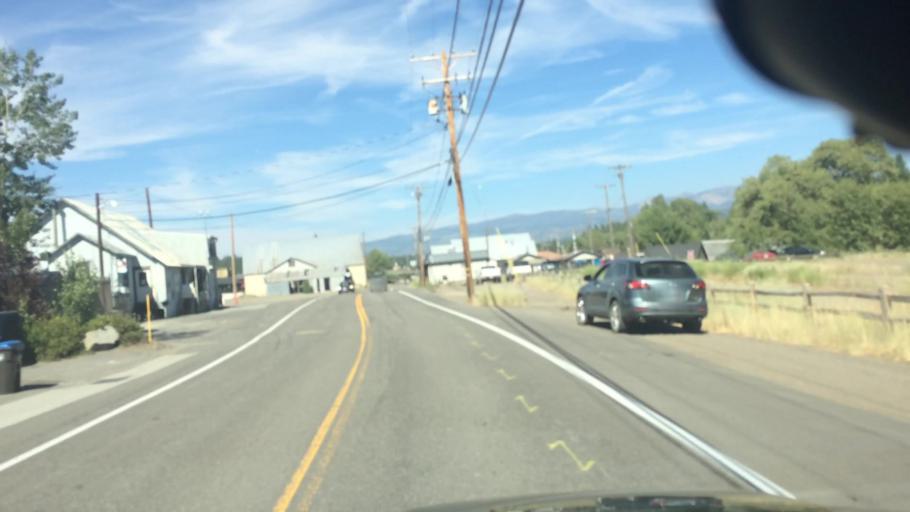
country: US
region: California
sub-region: Nevada County
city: Truckee
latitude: 39.3258
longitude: -120.1884
